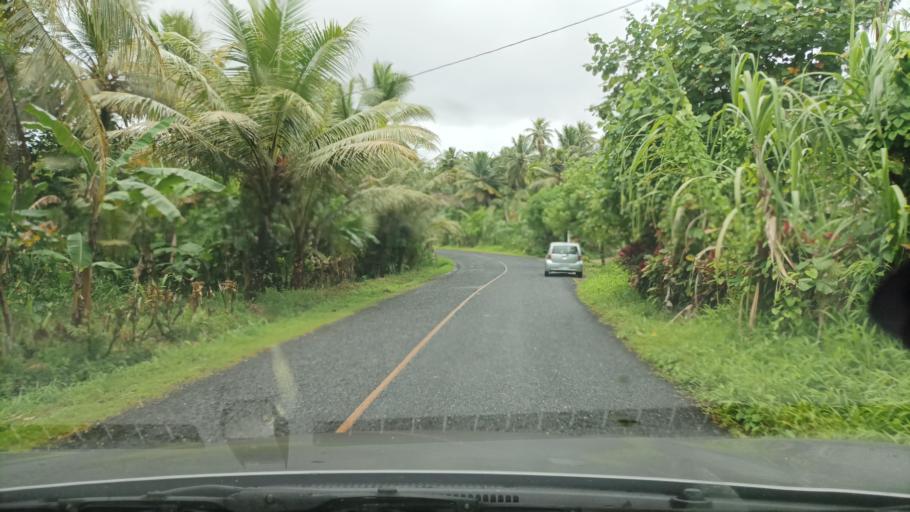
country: FM
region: Pohnpei
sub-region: Madolenihm Municipality
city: Madolenihm Municipality Government
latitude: 6.8102
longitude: 158.2485
